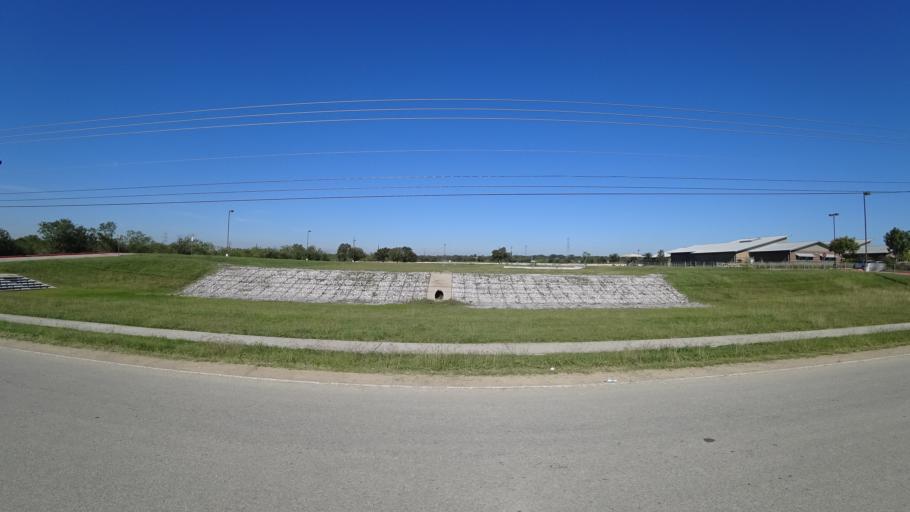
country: US
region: Texas
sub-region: Travis County
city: Hornsby Bend
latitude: 30.2563
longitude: -97.5926
